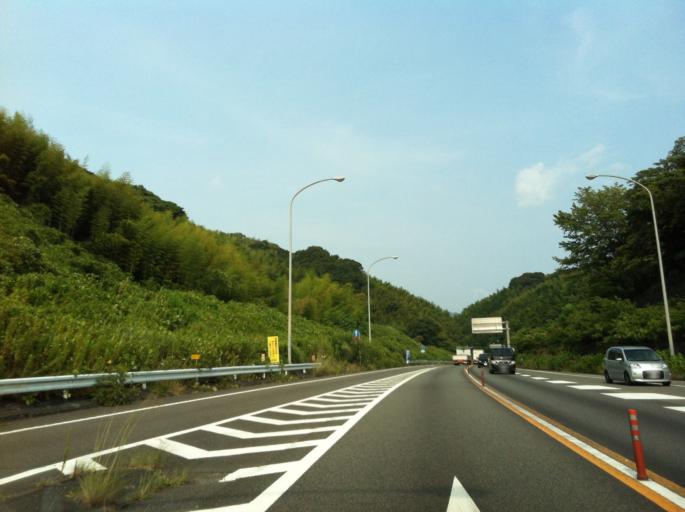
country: JP
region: Shizuoka
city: Fujieda
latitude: 34.8928
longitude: 138.2652
